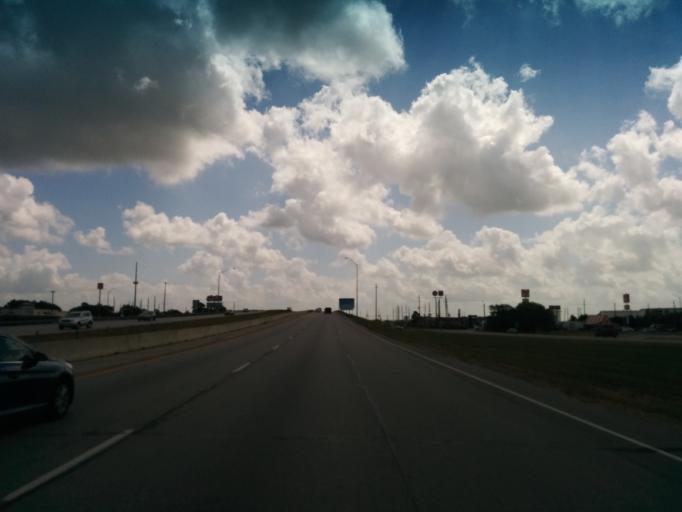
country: US
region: Texas
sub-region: Austin County
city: Sealy
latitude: 29.7637
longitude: -96.1551
